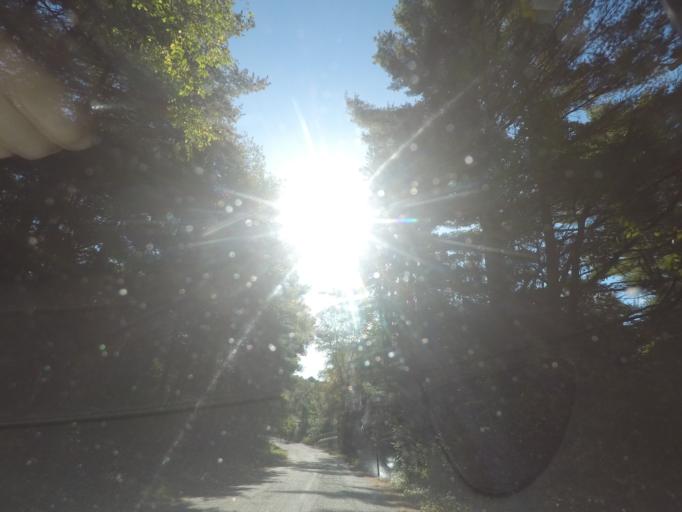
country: US
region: Connecticut
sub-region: Windham County
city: Thompson
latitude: 41.9729
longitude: -71.8264
